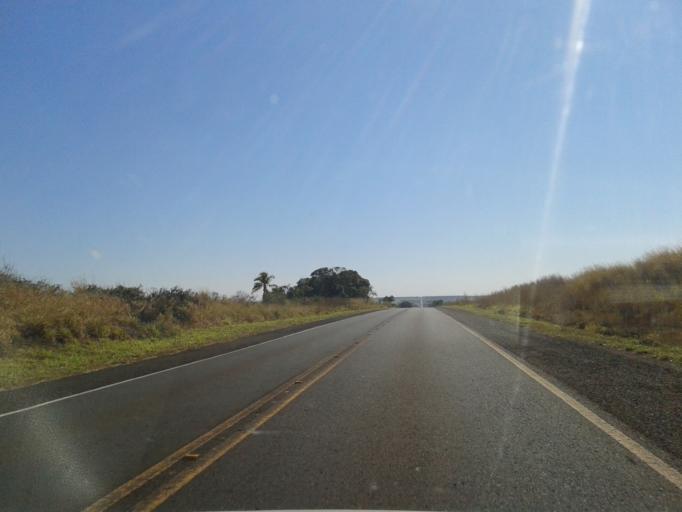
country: BR
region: Minas Gerais
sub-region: Santa Vitoria
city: Santa Vitoria
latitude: -19.0907
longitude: -50.3455
